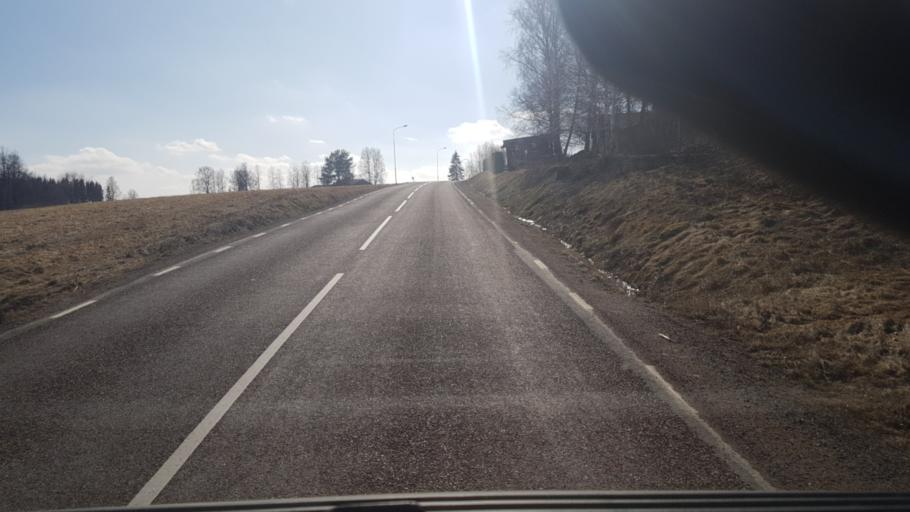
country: SE
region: Vaermland
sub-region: Eda Kommun
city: Charlottenberg
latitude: 59.8870
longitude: 12.3318
